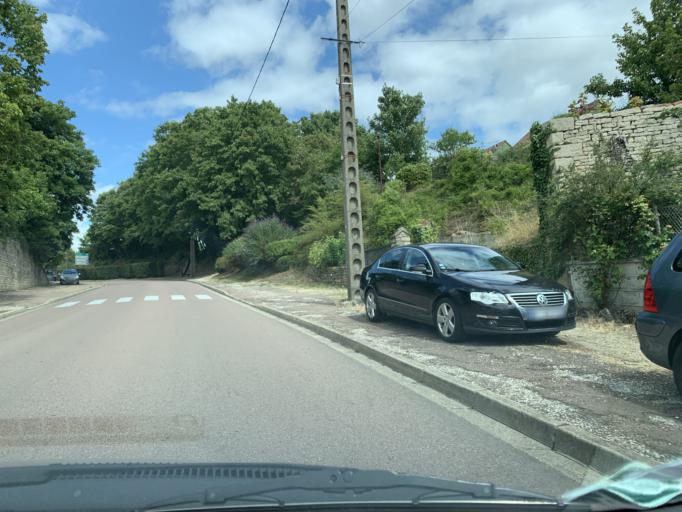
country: FR
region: Bourgogne
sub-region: Departement de la Nievre
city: Varzy
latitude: 47.3581
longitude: 3.3893
